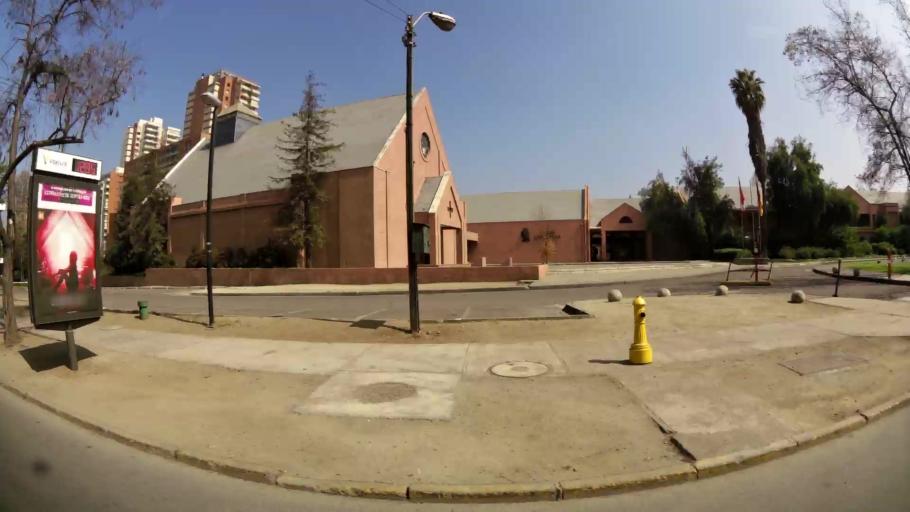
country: CL
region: Santiago Metropolitan
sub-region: Provincia de Santiago
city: Villa Presidente Frei, Nunoa, Santiago, Chile
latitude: -33.3941
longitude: -70.5972
